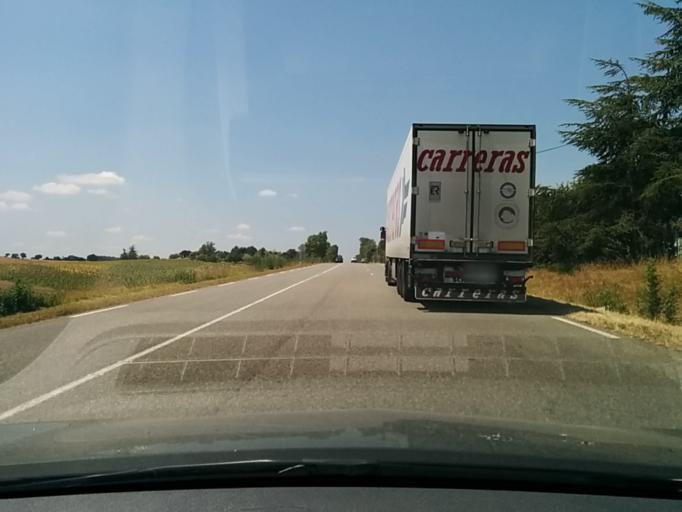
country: FR
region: Midi-Pyrenees
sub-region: Departement du Gers
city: Gimont
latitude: 43.6336
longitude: 0.8544
